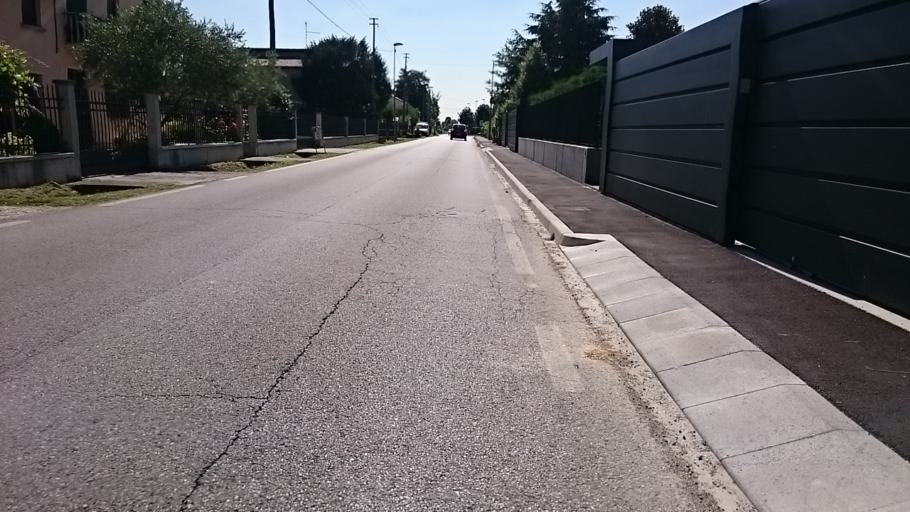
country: IT
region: Veneto
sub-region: Provincia di Padova
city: Veggiano
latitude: 45.4395
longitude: 11.6971
